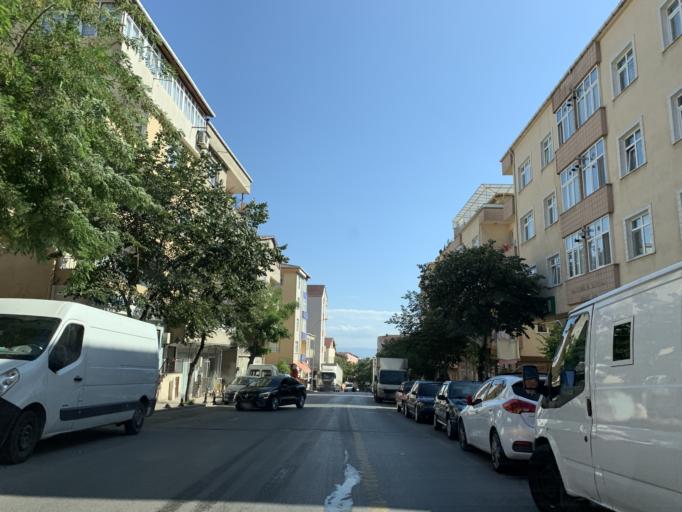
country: TR
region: Istanbul
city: Pendik
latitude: 40.8762
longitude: 29.2804
